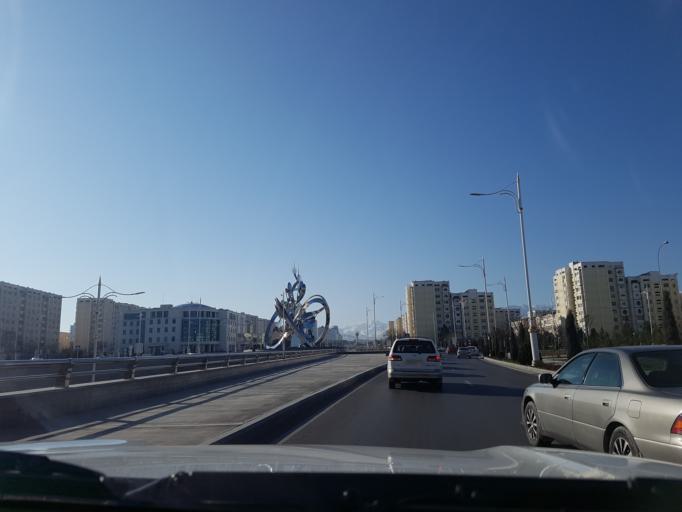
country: TM
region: Ahal
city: Ashgabat
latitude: 37.9035
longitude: 58.3887
